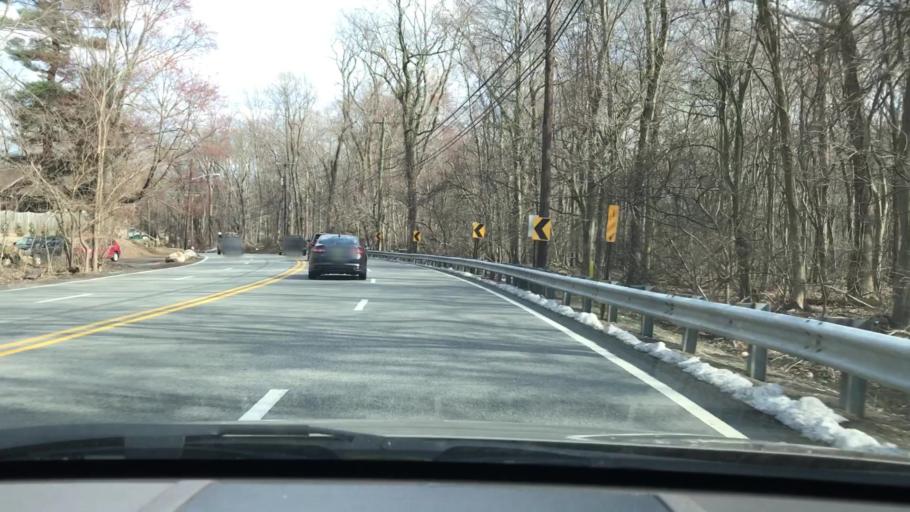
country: US
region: New Jersey
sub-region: Bergen County
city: Harrington Park
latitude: 40.9788
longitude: -73.9989
